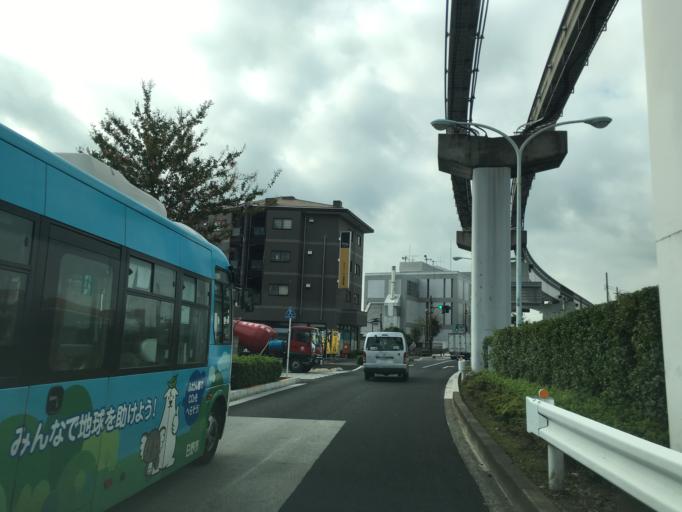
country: JP
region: Tokyo
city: Hino
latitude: 35.6692
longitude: 139.4208
